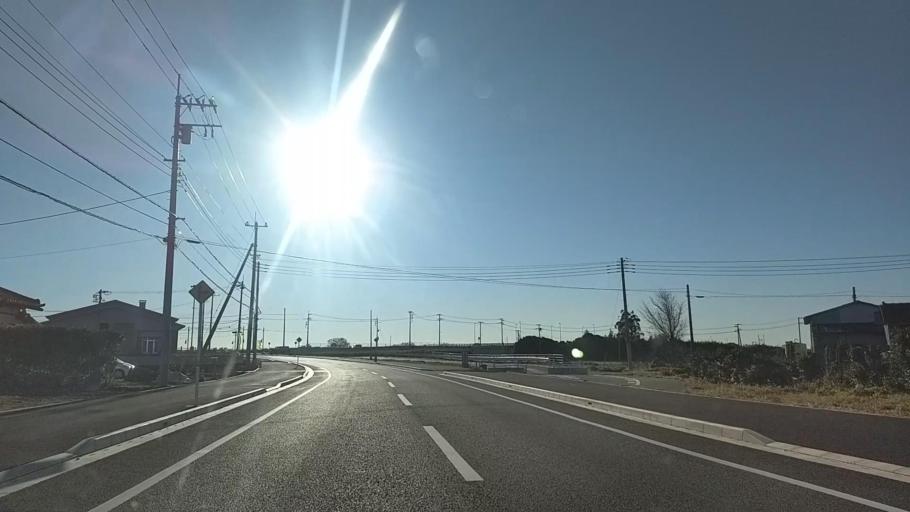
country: JP
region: Chiba
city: Kisarazu
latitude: 35.4240
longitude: 139.9178
